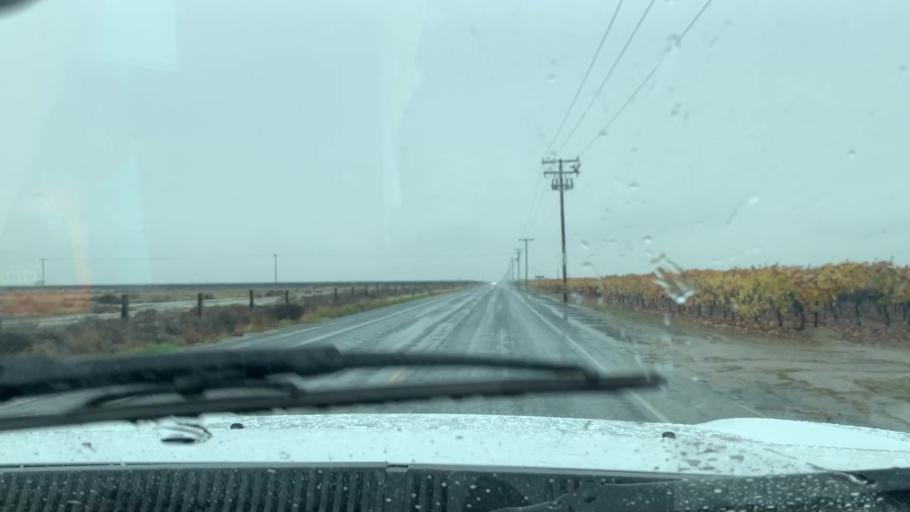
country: US
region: California
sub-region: Tulare County
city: Earlimart
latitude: 35.8919
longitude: -119.2832
